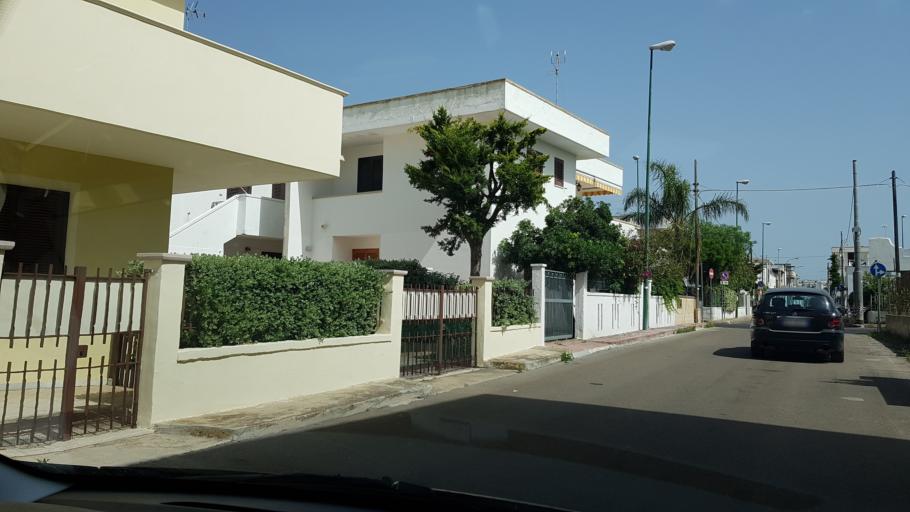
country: IT
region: Apulia
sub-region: Provincia di Lecce
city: Porto Cesareo
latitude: 40.2656
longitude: 17.8897
